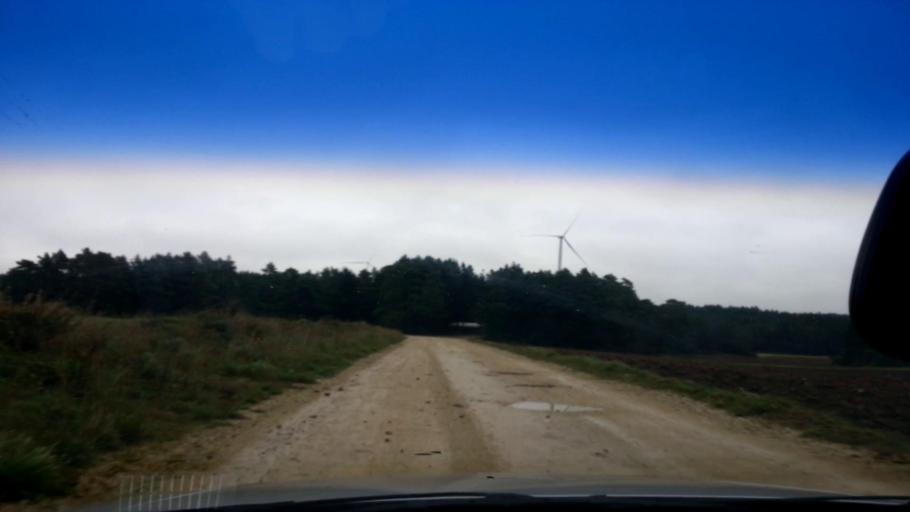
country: DE
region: Bavaria
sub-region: Upper Franconia
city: Wattendorf
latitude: 50.0126
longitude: 11.1498
